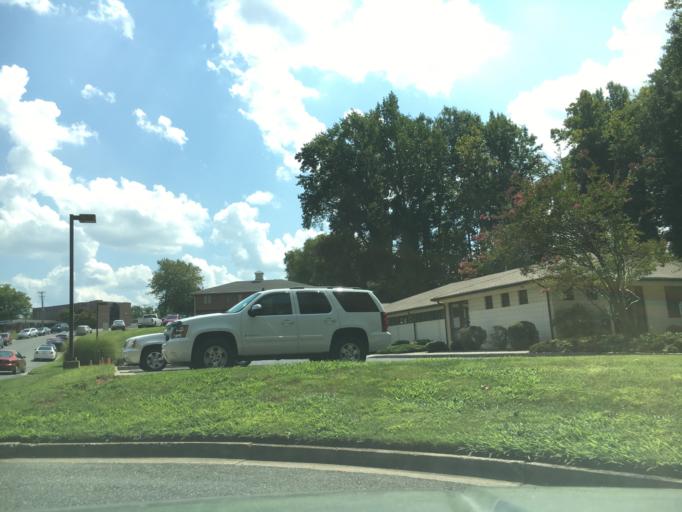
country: US
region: Virginia
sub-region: City of Lynchburg
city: West Lynchburg
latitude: 37.4149
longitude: -79.1751
